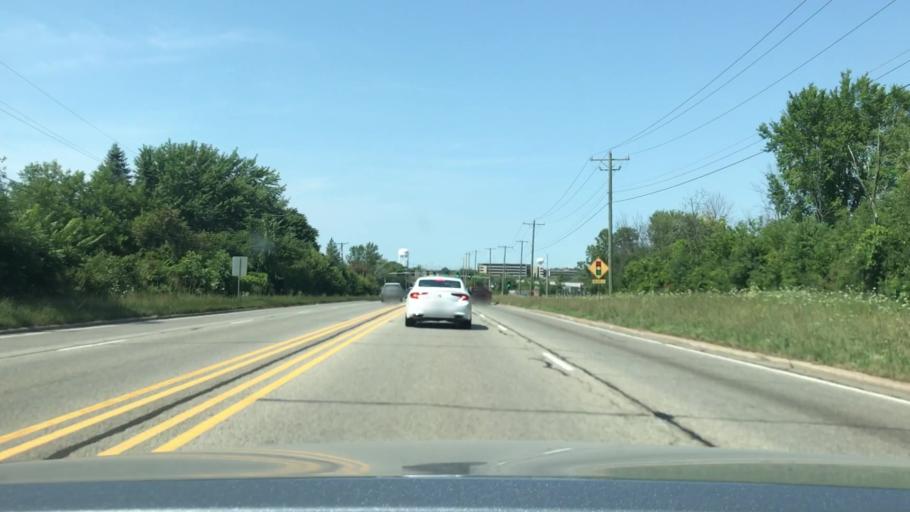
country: US
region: Illinois
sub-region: Kane County
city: Batavia
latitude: 41.8517
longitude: -88.2787
